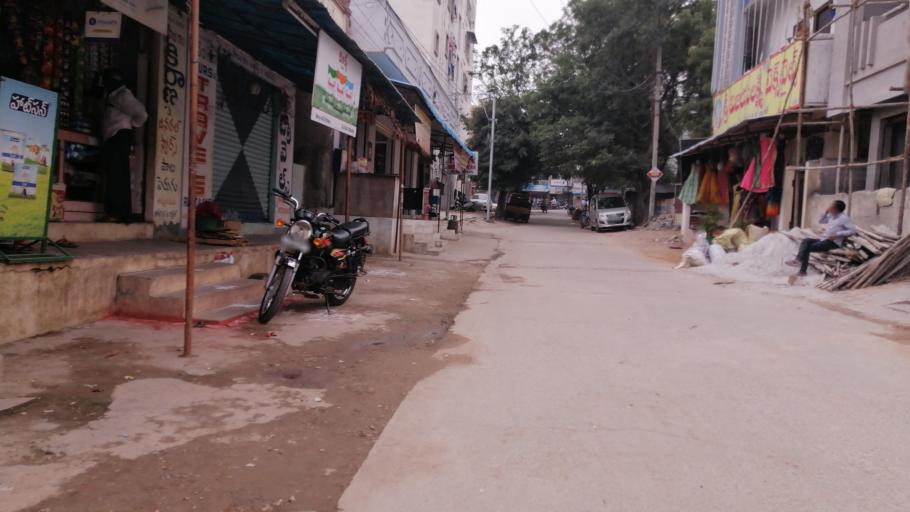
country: IN
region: Telangana
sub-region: Rangareddi
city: Secunderabad
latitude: 17.4810
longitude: 78.5807
